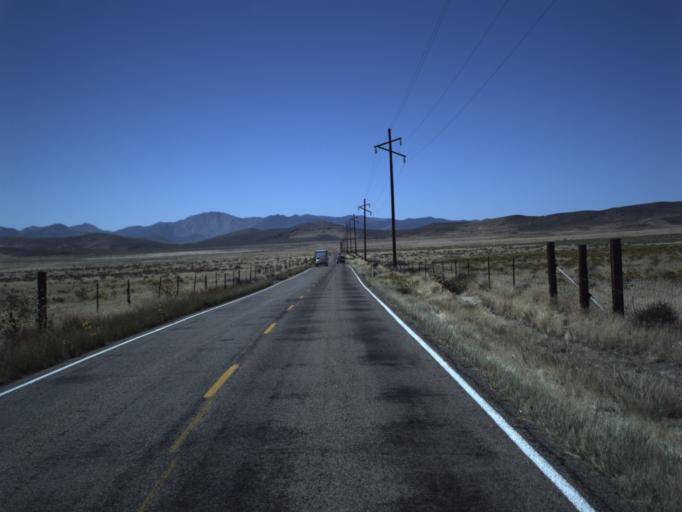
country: US
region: Utah
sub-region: Utah County
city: Eagle Mountain
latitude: 40.1665
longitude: -111.9418
